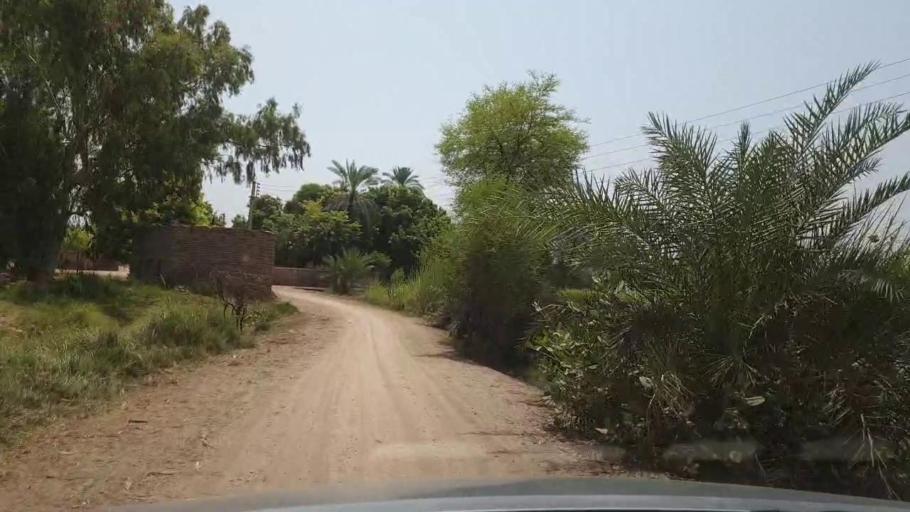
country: PK
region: Sindh
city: Ratodero
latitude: 27.7944
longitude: 68.3471
